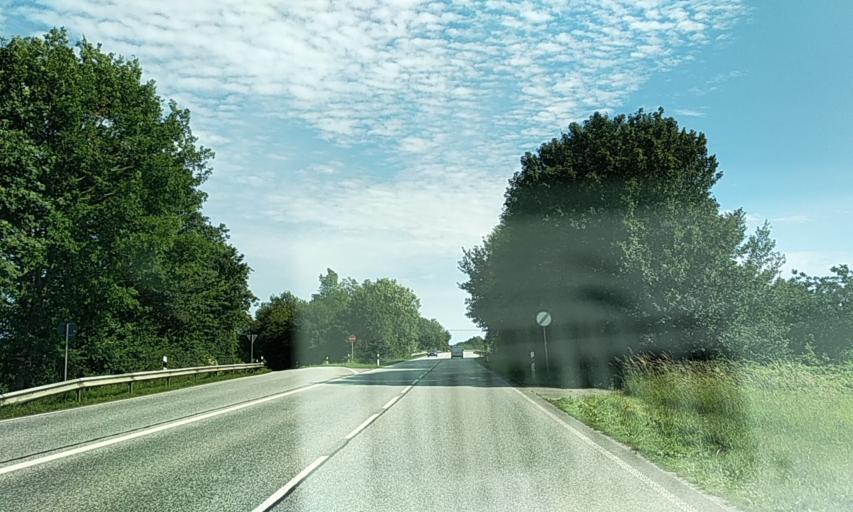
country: DE
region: Schleswig-Holstein
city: Busdorf
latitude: 54.4792
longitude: 9.5467
